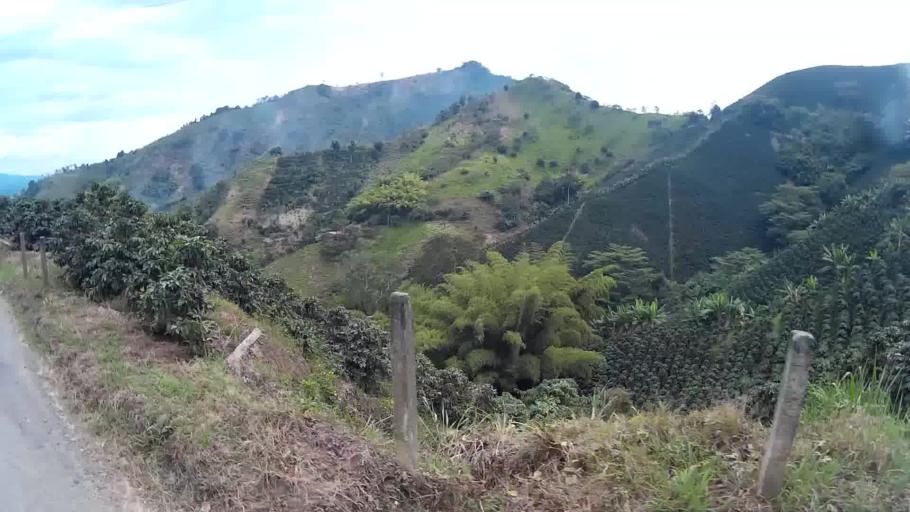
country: CO
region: Risaralda
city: Marsella
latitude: 4.8702
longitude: -75.7612
